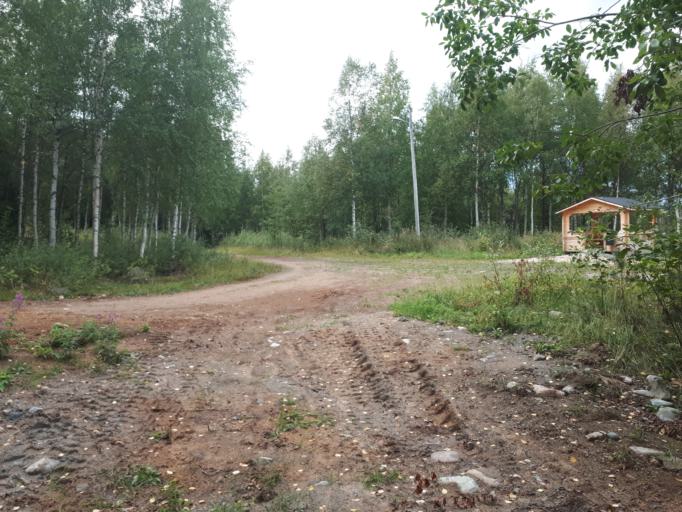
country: FI
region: Northern Ostrobothnia
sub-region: Oulunkaari
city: Ii
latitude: 65.3303
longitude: 25.4101
